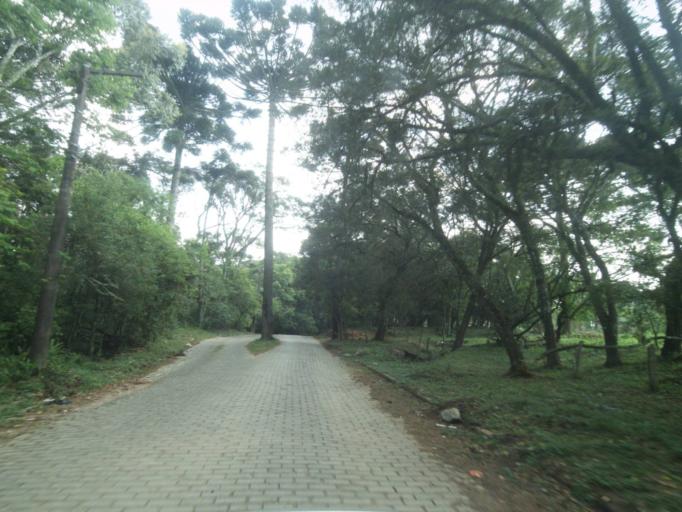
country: BR
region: Parana
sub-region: Sao Jose Dos Pinhais
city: Sao Jose dos Pinhais
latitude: -25.5444
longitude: -49.2385
